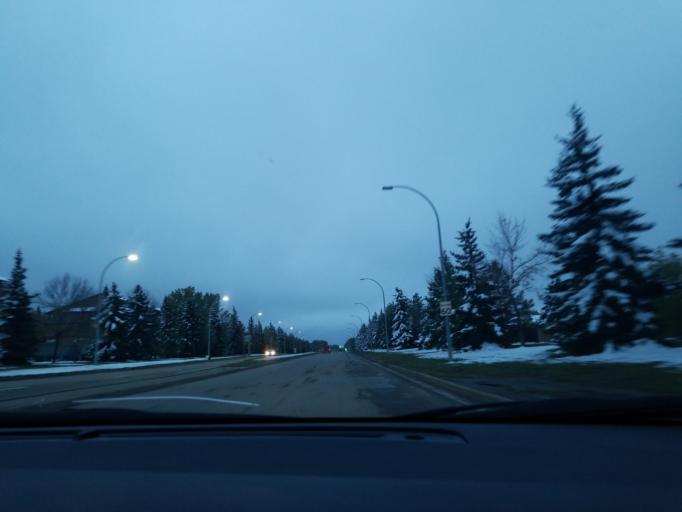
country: CA
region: Alberta
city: Edmonton
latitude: 53.6131
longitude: -113.3801
